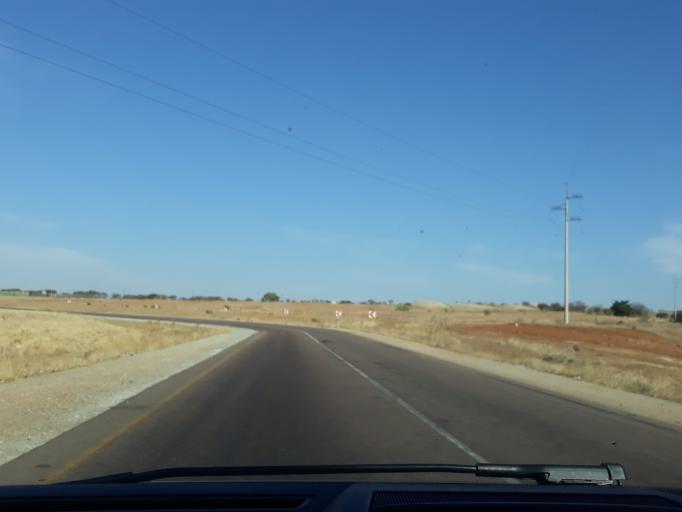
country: ZA
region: Limpopo
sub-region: Capricorn District Municipality
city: Polokwane
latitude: -23.9435
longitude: 29.4188
